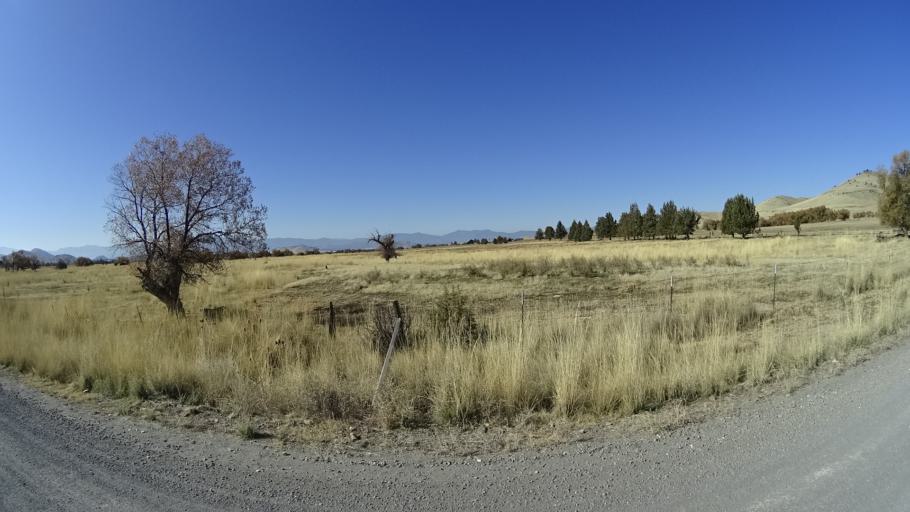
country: US
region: California
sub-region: Siskiyou County
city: Montague
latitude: 41.7257
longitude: -122.3696
